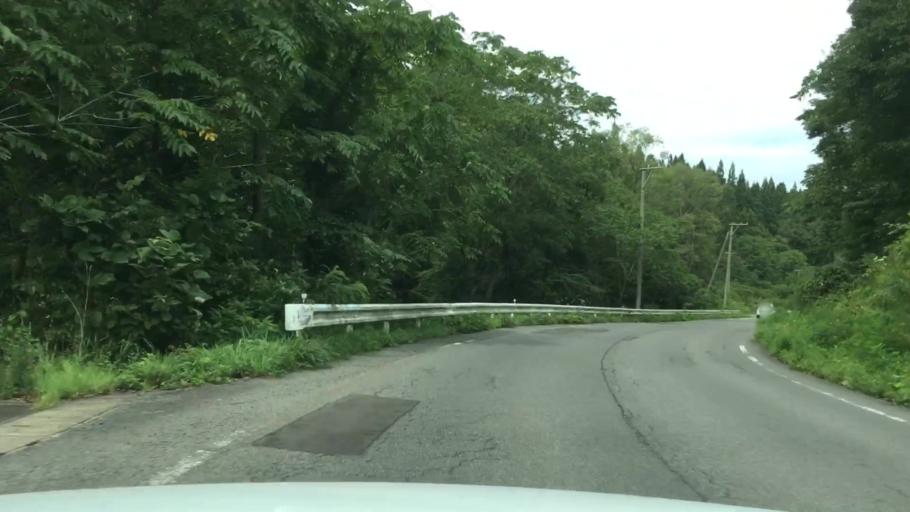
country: JP
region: Aomori
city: Shimokizukuri
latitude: 40.7254
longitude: 140.2547
